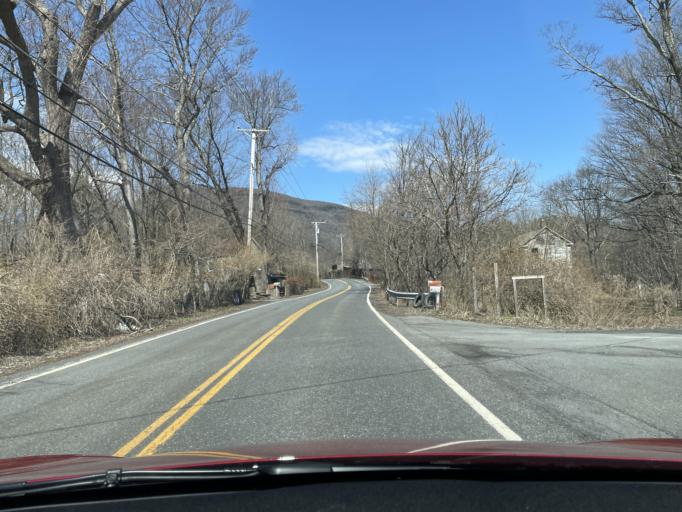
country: US
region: New York
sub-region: Ulster County
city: Manorville
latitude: 42.1109
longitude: -74.0458
